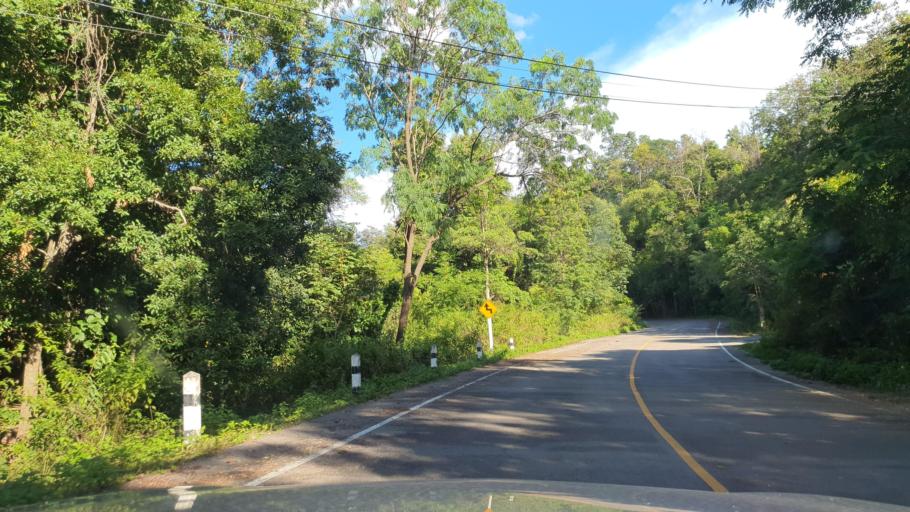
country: TH
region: Chiang Mai
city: Mae On
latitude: 18.7894
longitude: 99.3036
